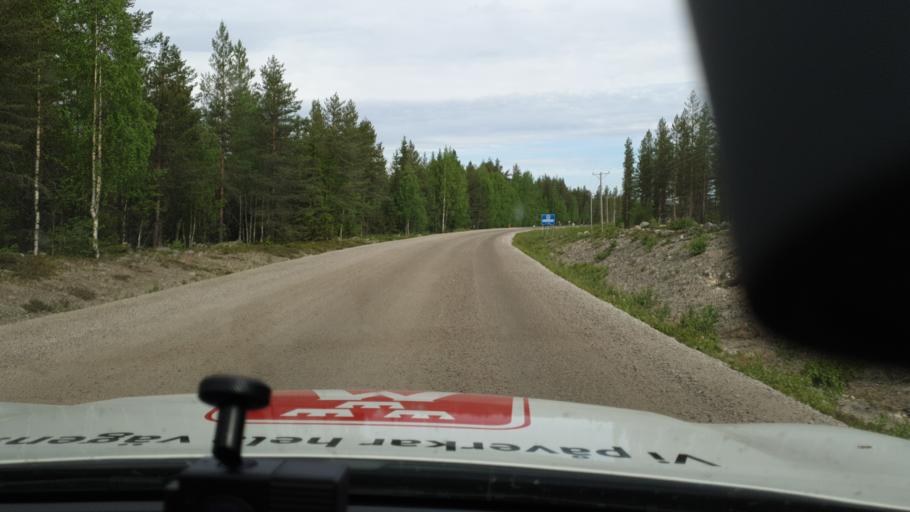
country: SE
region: Vaesterbotten
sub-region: Lycksele Kommun
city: Lycksele
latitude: 64.8602
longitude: 18.7251
